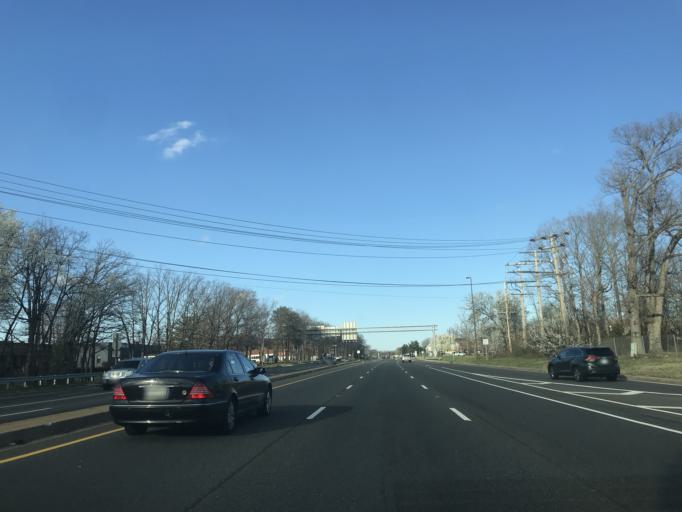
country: US
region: Maryland
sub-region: Prince George's County
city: Springdale
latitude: 38.9493
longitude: -76.8400
